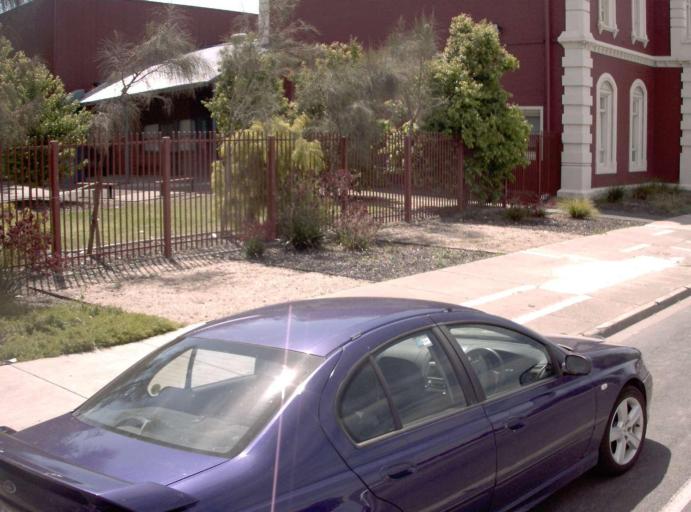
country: AU
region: Victoria
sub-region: Wellington
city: Sale
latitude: -38.1086
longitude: 147.0682
